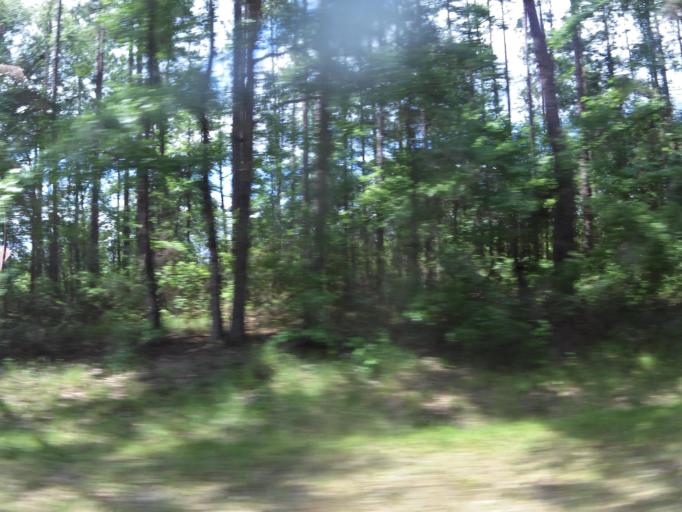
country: US
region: Florida
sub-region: Clay County
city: Asbury Lake
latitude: 29.9131
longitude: -81.8918
